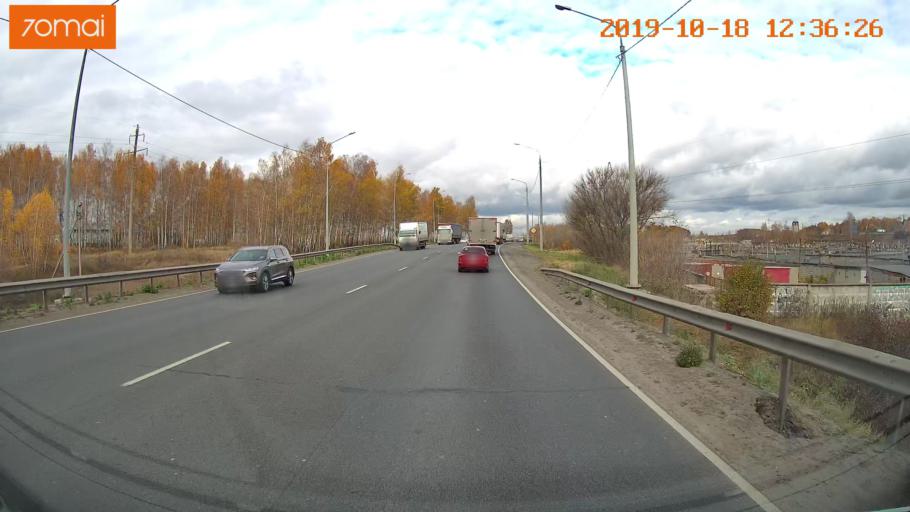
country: RU
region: Rjazan
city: Ryazan'
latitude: 54.6349
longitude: 39.6336
